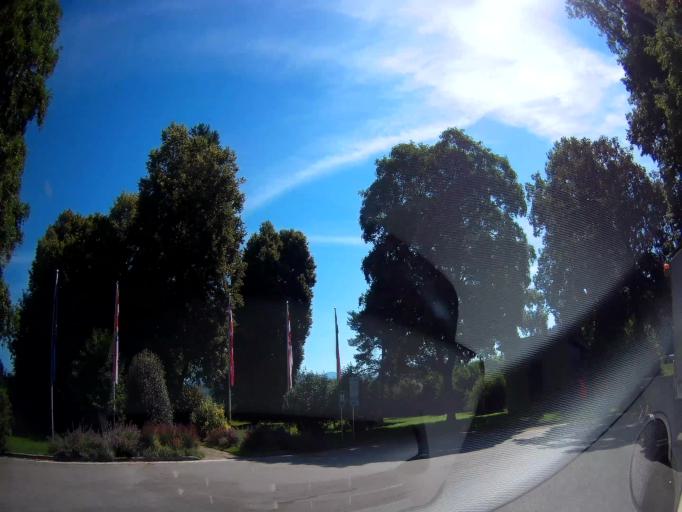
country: AT
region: Carinthia
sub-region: Politischer Bezirk Klagenfurt Land
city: Maria Saal
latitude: 46.6905
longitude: 14.3460
